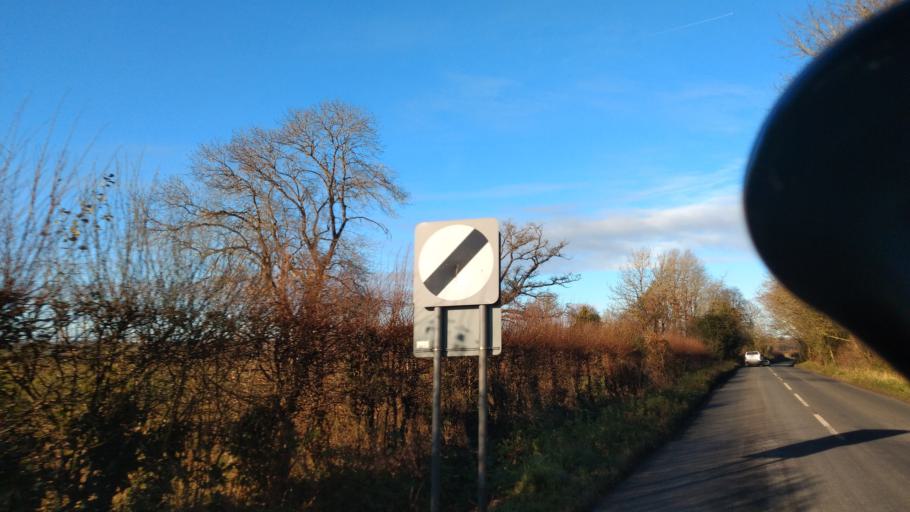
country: GB
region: England
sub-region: Wiltshire
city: Wingfield
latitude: 51.3161
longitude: -2.2578
